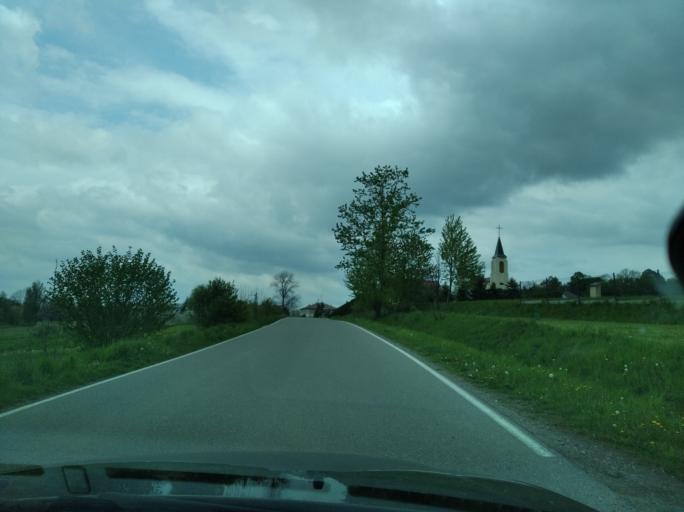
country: PL
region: Subcarpathian Voivodeship
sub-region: Powiat brzozowski
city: Turze Pole
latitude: 49.6378
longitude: 22.0025
